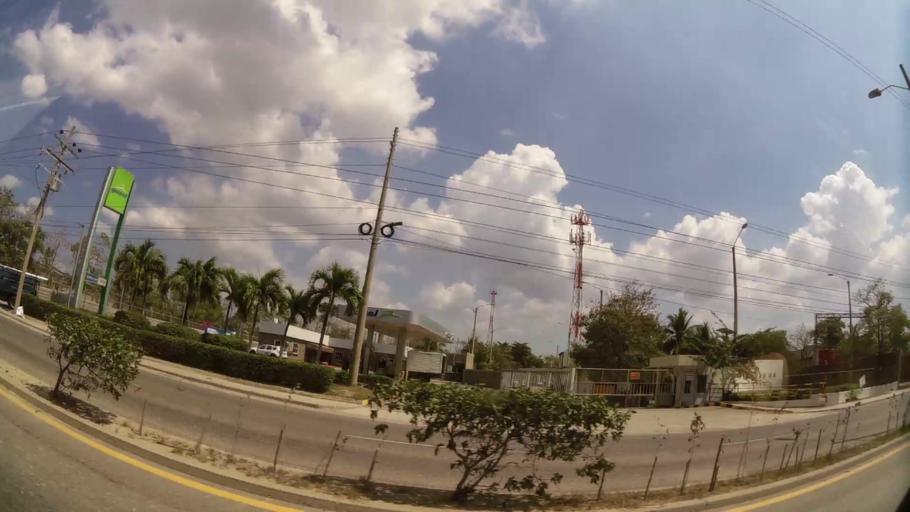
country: CO
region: Bolivar
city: Cartagena
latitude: 10.3499
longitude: -75.4954
